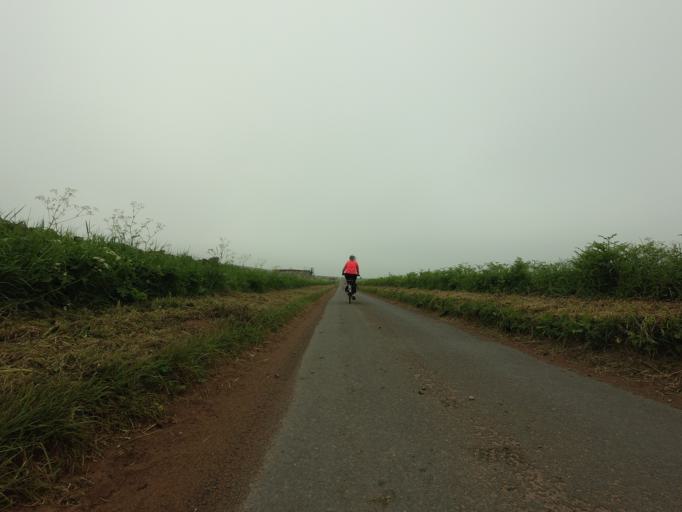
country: GB
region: Scotland
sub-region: Perth and Kinross
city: Abernethy
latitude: 56.2597
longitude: -3.3162
